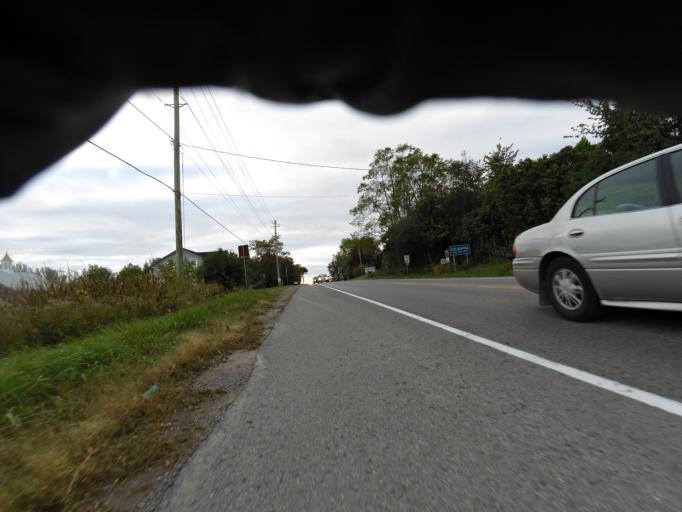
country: CA
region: Ontario
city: Cobourg
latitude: 44.0112
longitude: -77.8632
